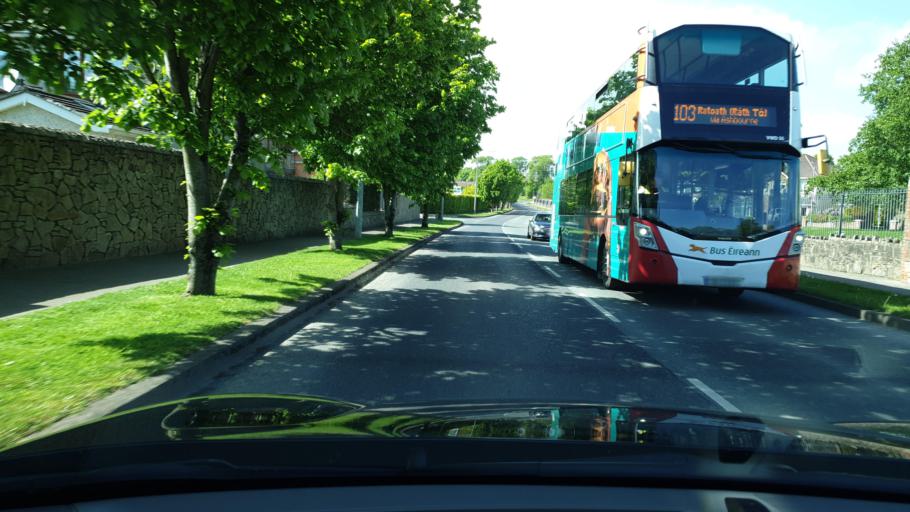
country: IE
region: Leinster
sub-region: An Mhi
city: Ratoath
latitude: 53.5062
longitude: -6.4688
